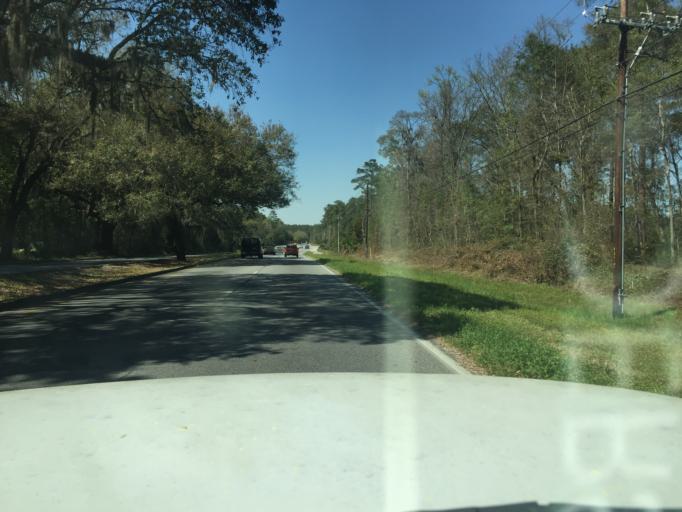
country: US
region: Georgia
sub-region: Chatham County
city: Whitemarsh Island
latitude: 32.0294
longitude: -81.0025
